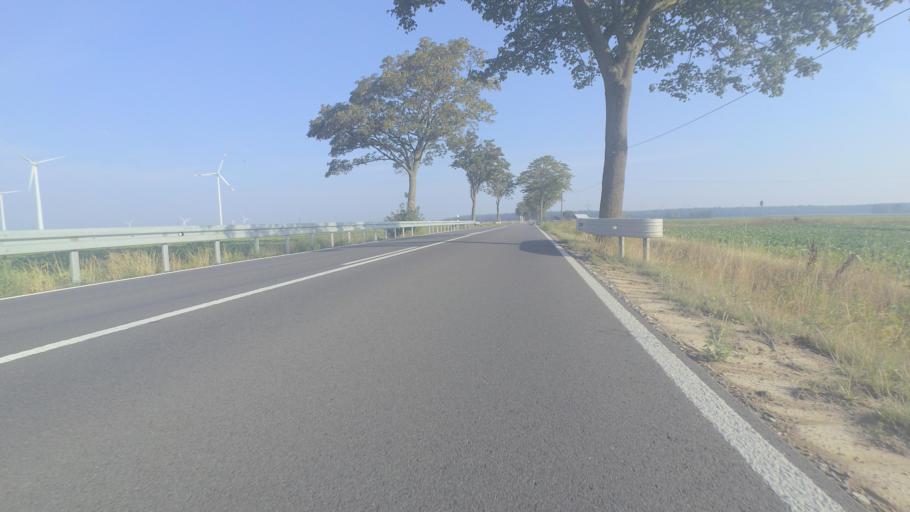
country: DE
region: Mecklenburg-Vorpommern
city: Gormin
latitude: 54.0099
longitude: 13.1416
